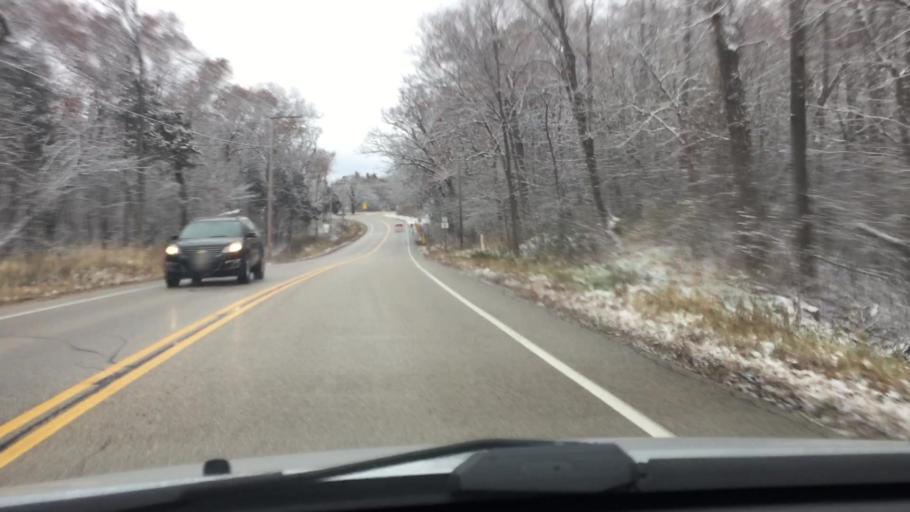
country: US
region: Wisconsin
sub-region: Waukesha County
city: Dousman
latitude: 42.9814
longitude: -88.4653
